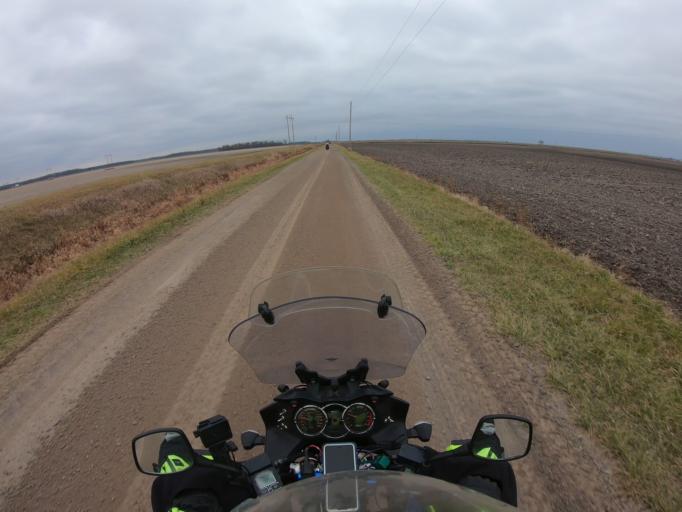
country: US
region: Michigan
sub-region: Saginaw County
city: Burt
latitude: 43.2634
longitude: -83.9772
